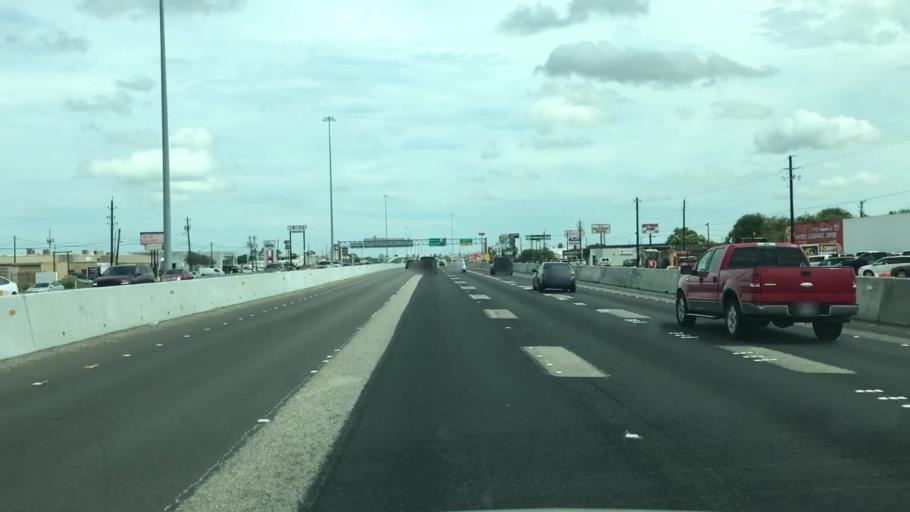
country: US
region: Texas
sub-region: Nueces County
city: Corpus Christi
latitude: 27.7316
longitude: -97.4194
